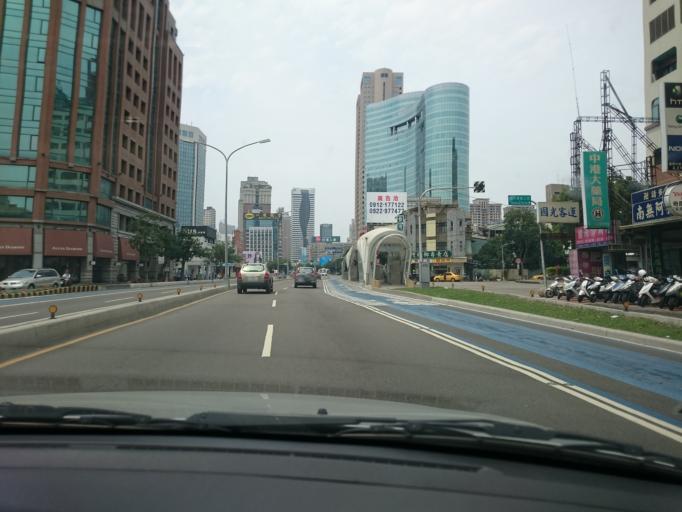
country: TW
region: Taiwan
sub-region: Taichung City
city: Taichung
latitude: 24.1496
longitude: 120.6713
